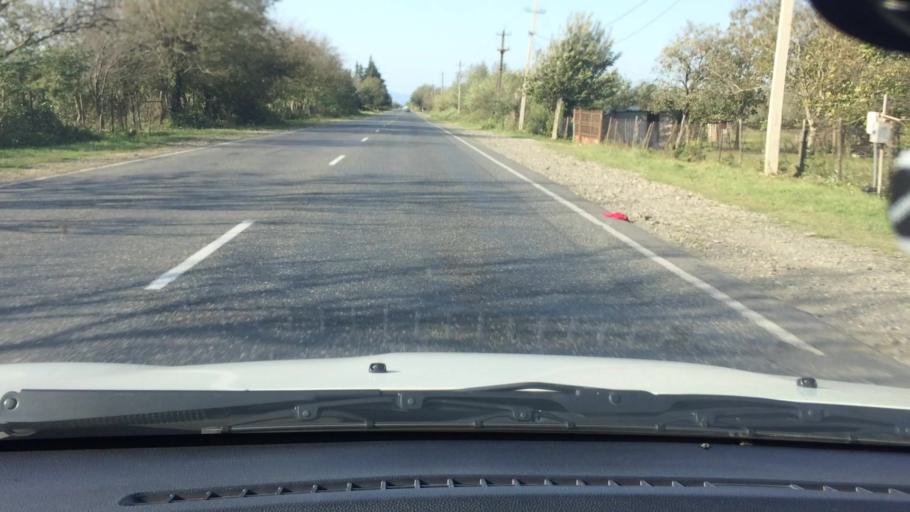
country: GE
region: Imereti
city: Tsqaltubo
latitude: 42.2164
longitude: 42.5684
